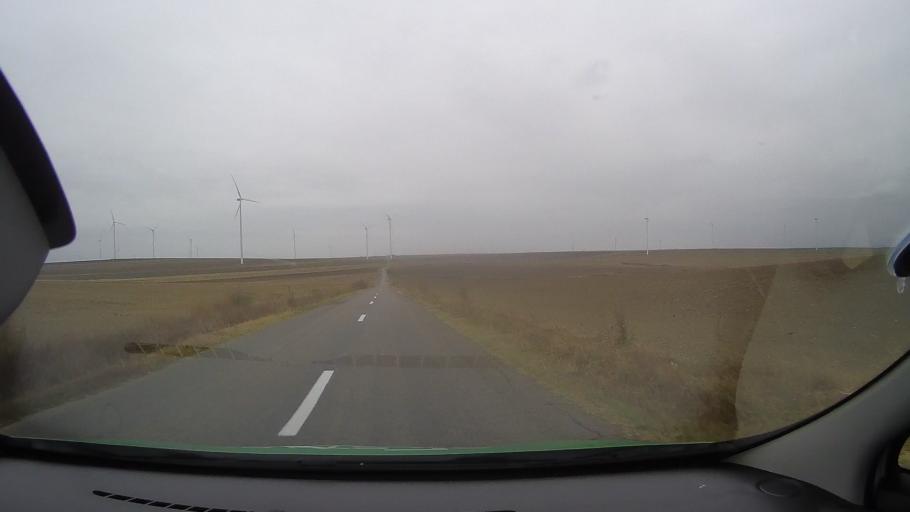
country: RO
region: Constanta
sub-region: Comuna Pantelimon
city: Pantelimon
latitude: 44.5126
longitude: 28.3357
